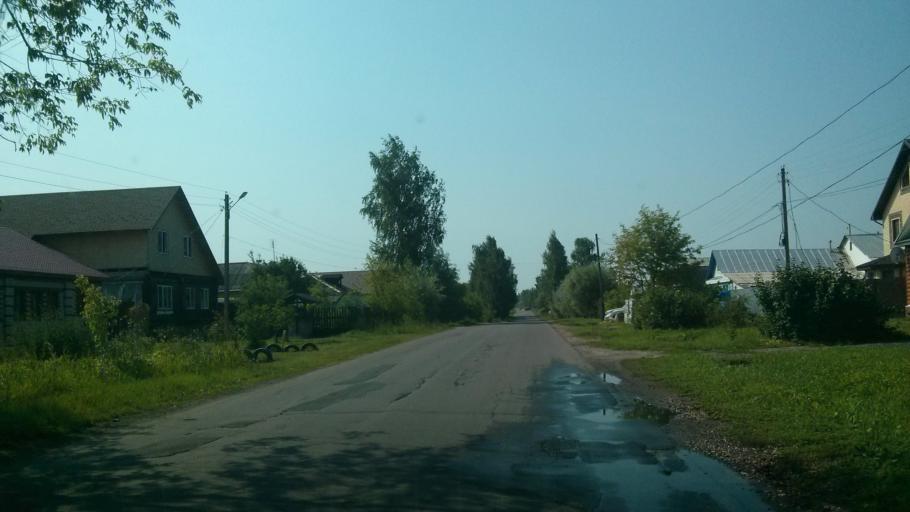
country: RU
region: Vladimir
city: Murom
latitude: 55.5386
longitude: 42.0248
